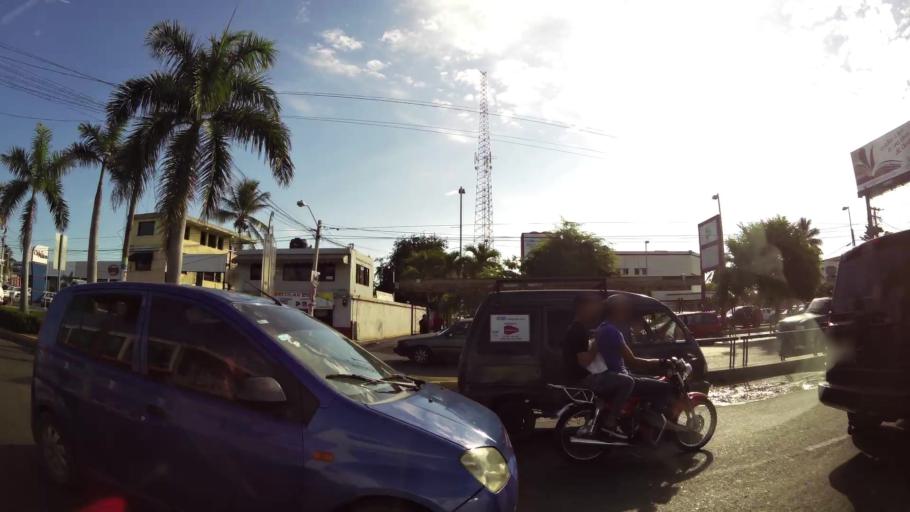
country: DO
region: Santo Domingo
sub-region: Santo Domingo
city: Santo Domingo Este
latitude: 18.4917
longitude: -69.8504
